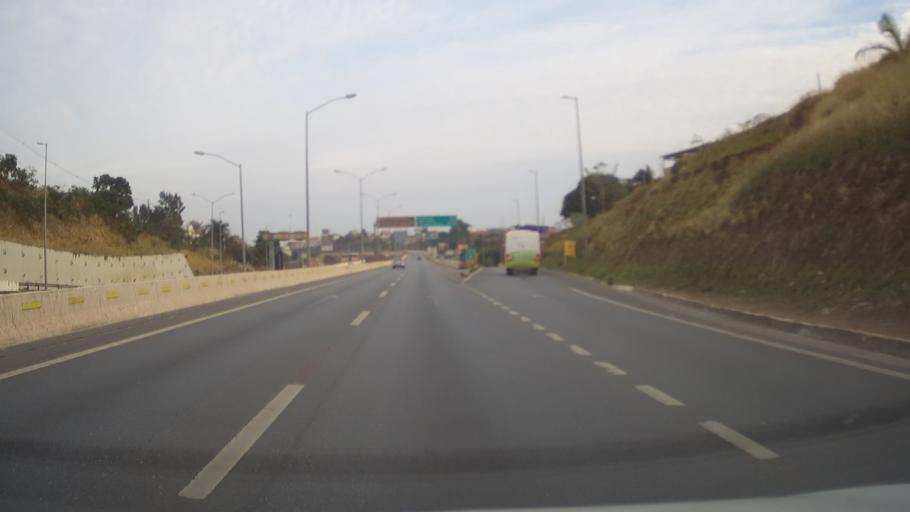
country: BR
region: Minas Gerais
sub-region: Vespasiano
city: Vespasiano
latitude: -19.7596
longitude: -43.9477
